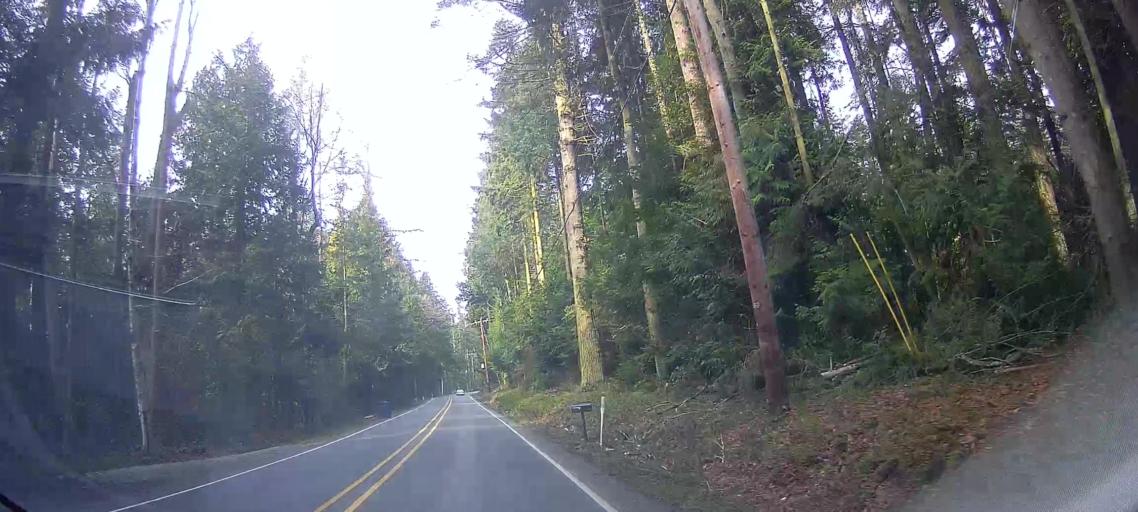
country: US
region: Washington
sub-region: Island County
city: Langley
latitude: 48.1166
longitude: -122.4495
